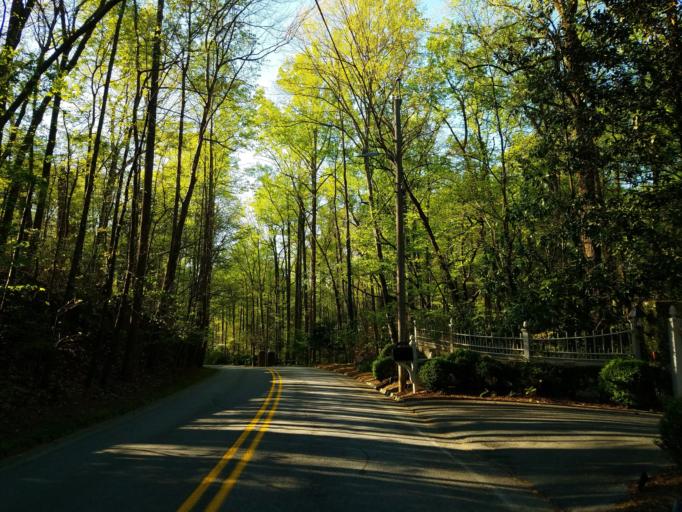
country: US
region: Georgia
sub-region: Cobb County
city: Vinings
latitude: 33.8407
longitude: -84.4565
